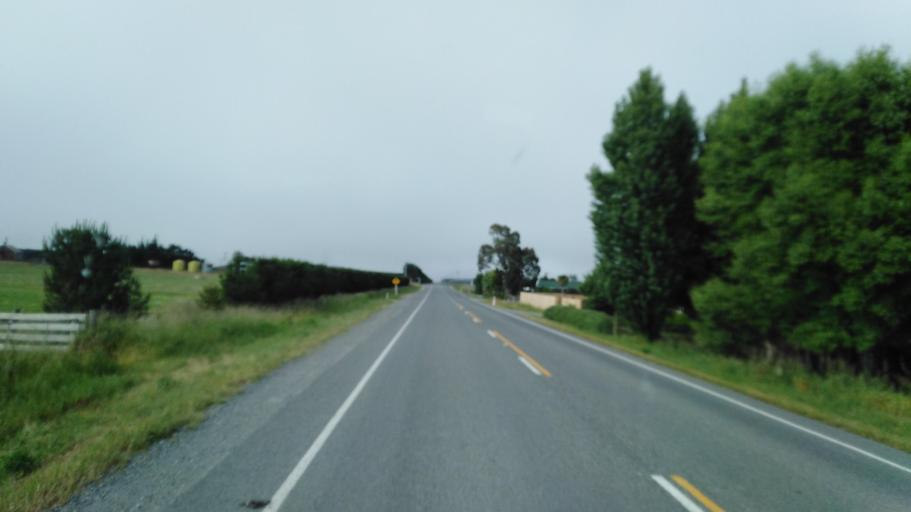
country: NZ
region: Canterbury
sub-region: Hurunui District
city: Amberley
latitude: -42.7991
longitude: 172.8281
